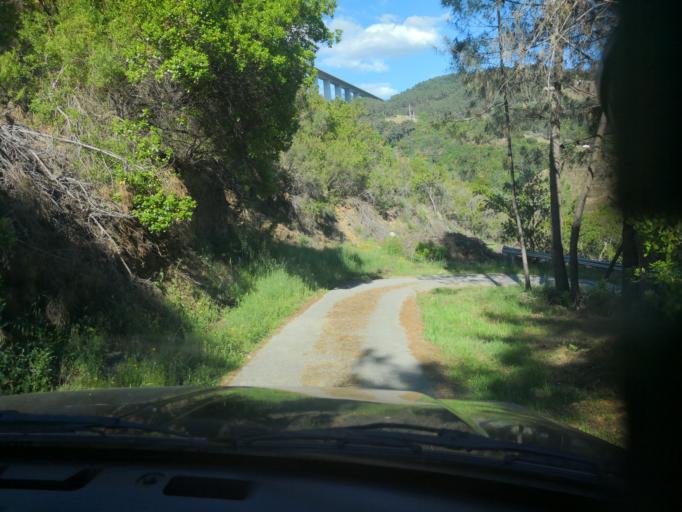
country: PT
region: Vila Real
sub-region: Vila Real
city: Vila Real
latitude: 41.2756
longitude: -7.7474
